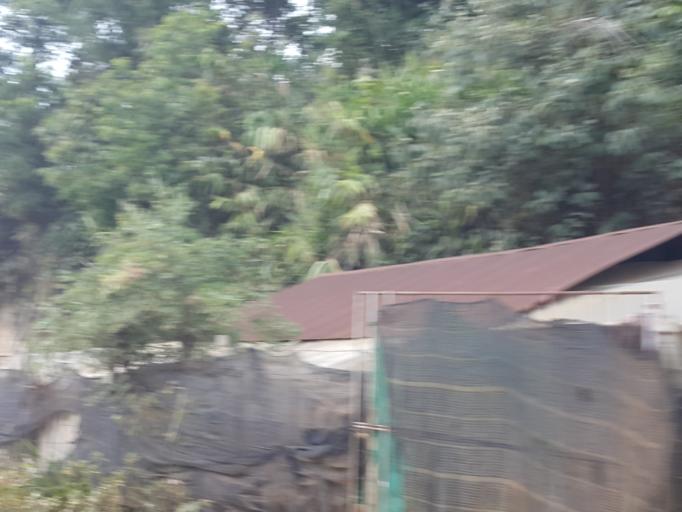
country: TH
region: Chiang Mai
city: Samoeng
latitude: 18.9347
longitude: 98.8211
